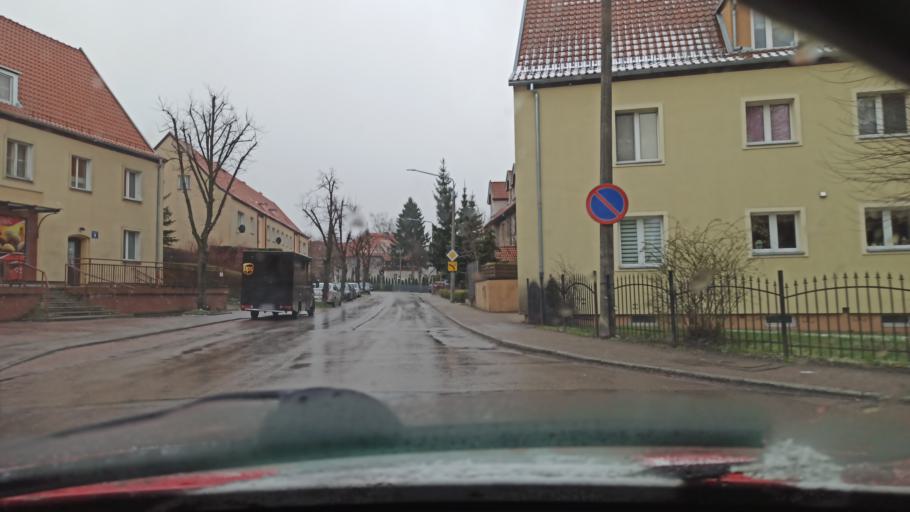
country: PL
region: Warmian-Masurian Voivodeship
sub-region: Powiat elblaski
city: Elblag
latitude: 54.1735
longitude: 19.4127
